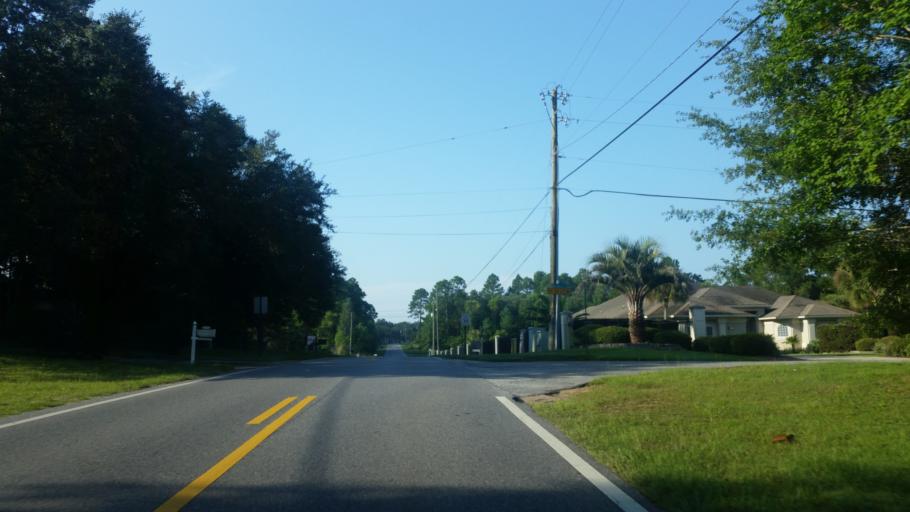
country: US
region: Florida
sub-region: Escambia County
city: Bellview
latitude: 30.5111
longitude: -87.3224
